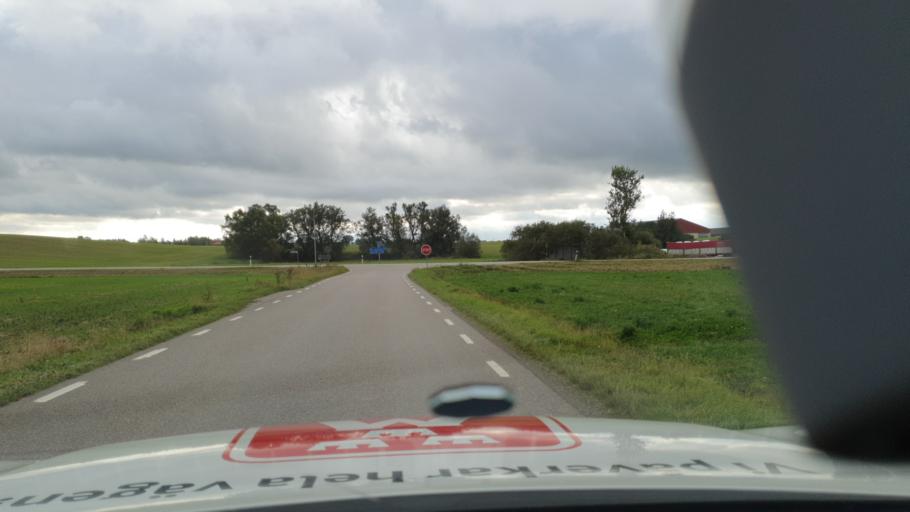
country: SE
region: Skane
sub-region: Svedala Kommun
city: Svedala
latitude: 55.4547
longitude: 13.1803
